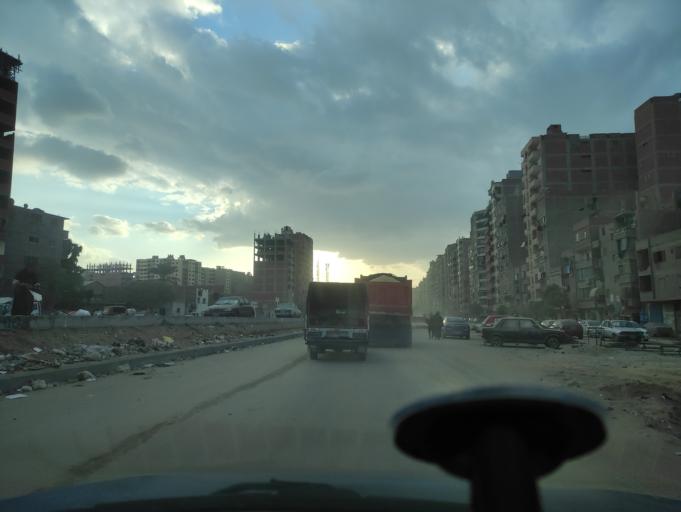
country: EG
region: Muhafazat al Qalyubiyah
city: Al Khankah
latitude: 30.1349
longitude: 31.3294
